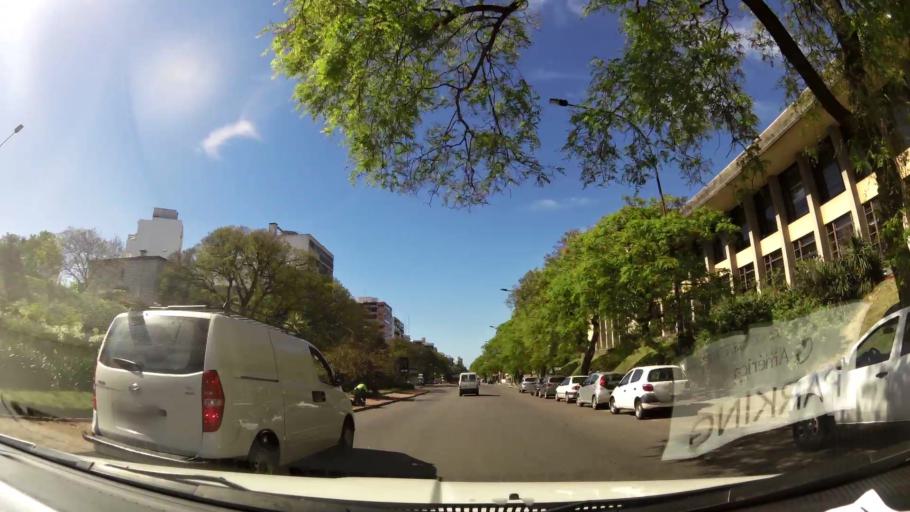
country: UY
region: Montevideo
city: Montevideo
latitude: -34.9101
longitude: -56.1634
